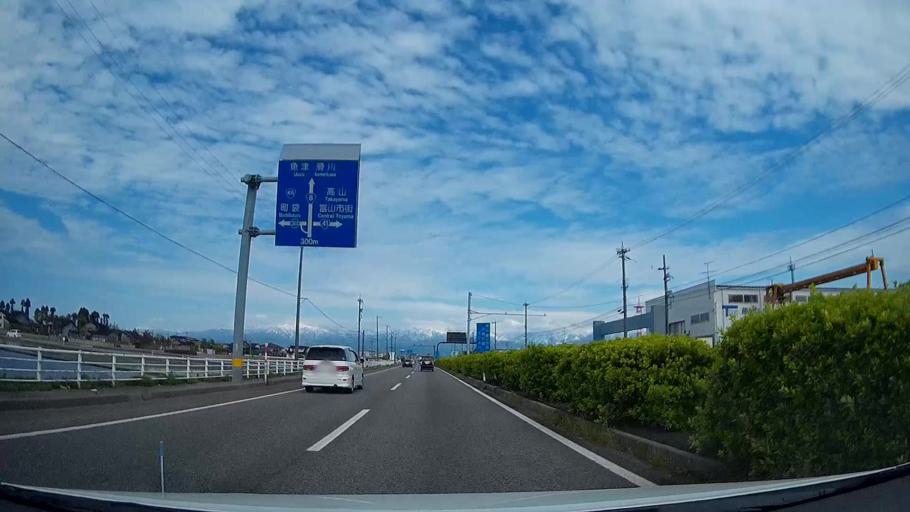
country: JP
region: Toyama
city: Toyama-shi
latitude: 36.7207
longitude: 137.2559
